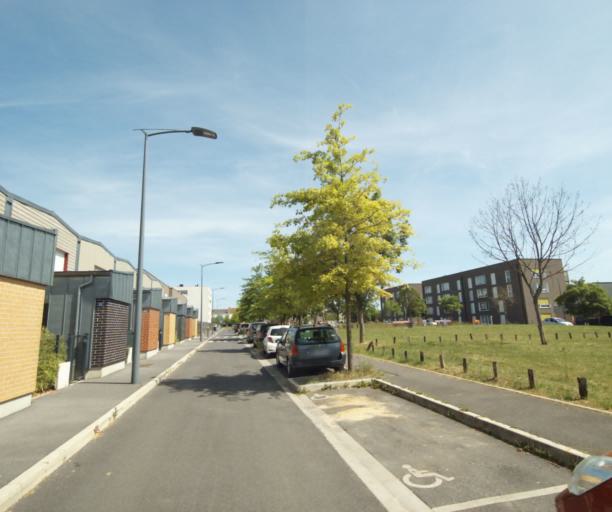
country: FR
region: Champagne-Ardenne
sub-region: Departement des Ardennes
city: Prix-les-Mezieres
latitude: 49.7654
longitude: 4.6876
